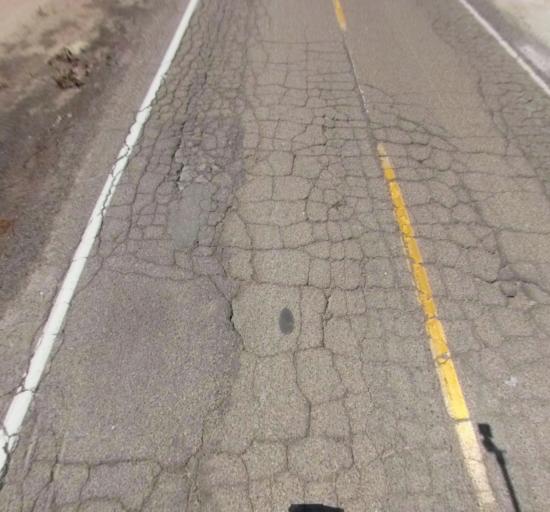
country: US
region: California
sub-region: Madera County
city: Madera
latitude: 36.9272
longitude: -120.2014
